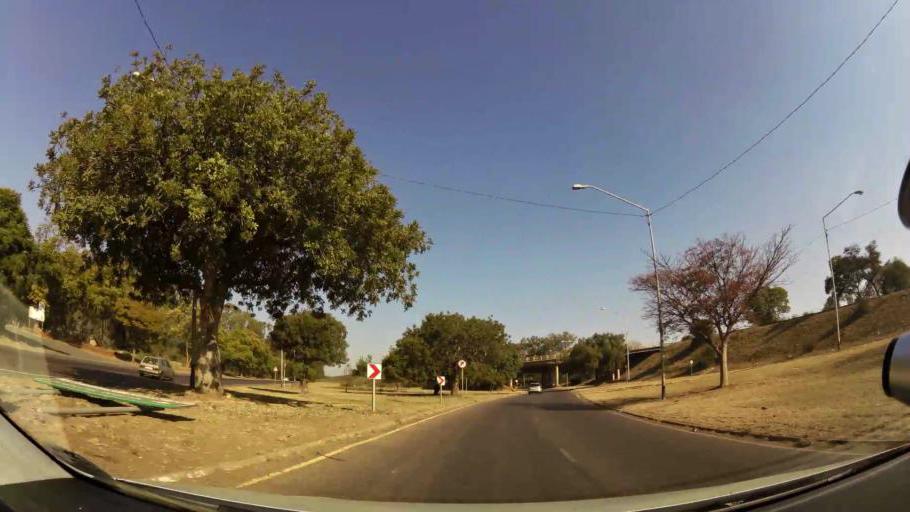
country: ZA
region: Gauteng
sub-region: City of Tshwane Metropolitan Municipality
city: Pretoria
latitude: -25.6661
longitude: 28.1830
